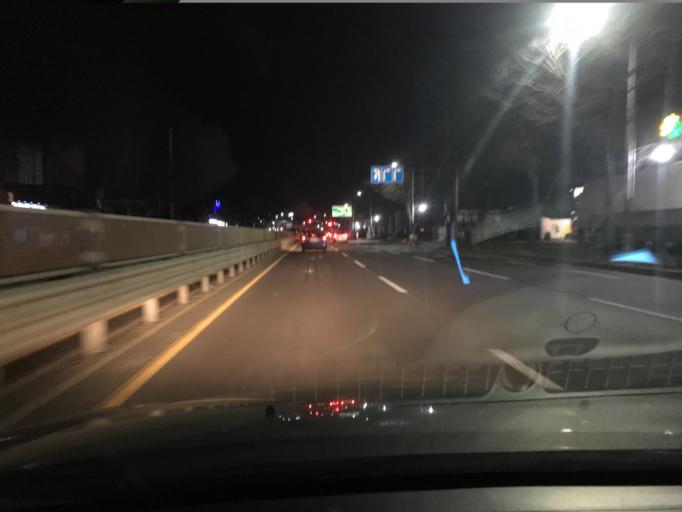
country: KR
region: Daegu
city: Hwawon
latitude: 35.6908
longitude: 128.4450
